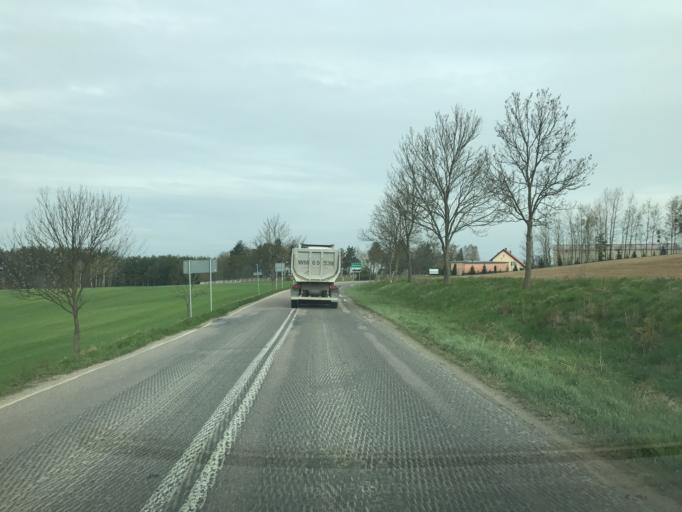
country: PL
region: Warmian-Masurian Voivodeship
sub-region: Powiat ostrodzki
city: Gierzwald
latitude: 53.5803
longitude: 20.0897
